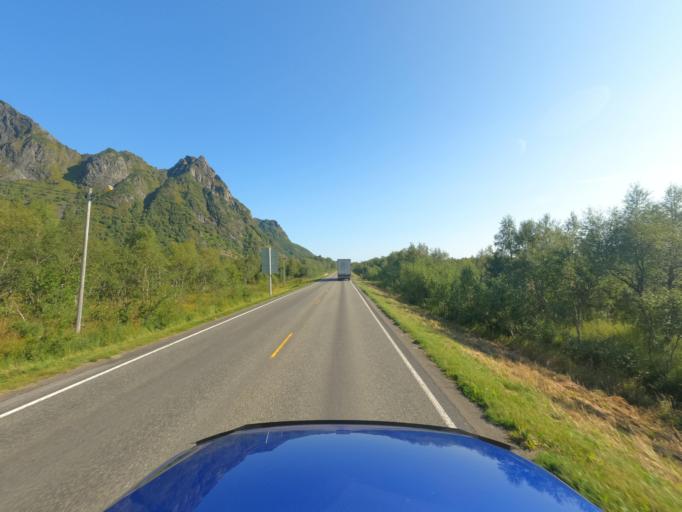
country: NO
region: Nordland
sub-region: Vagan
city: Kabelvag
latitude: 68.2120
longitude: 14.3674
